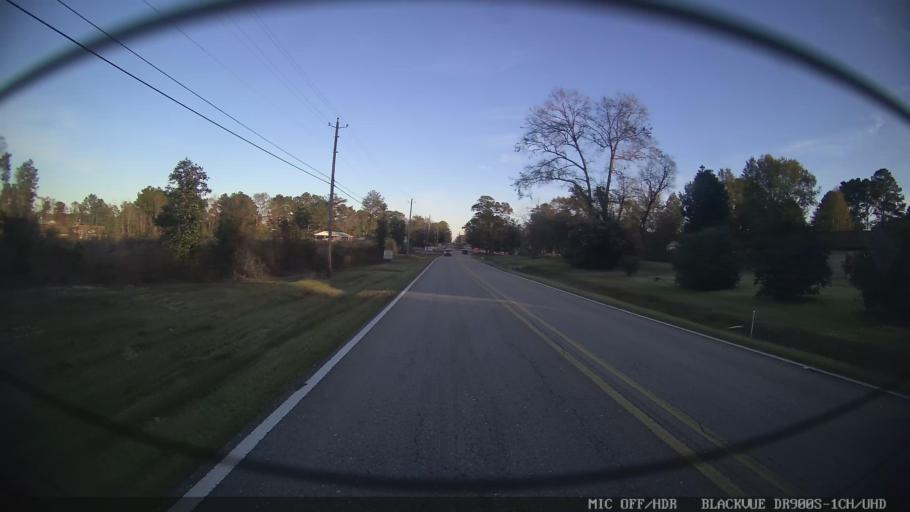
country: US
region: Mississippi
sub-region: Lamar County
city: Lumberton
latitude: 31.0070
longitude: -89.4672
